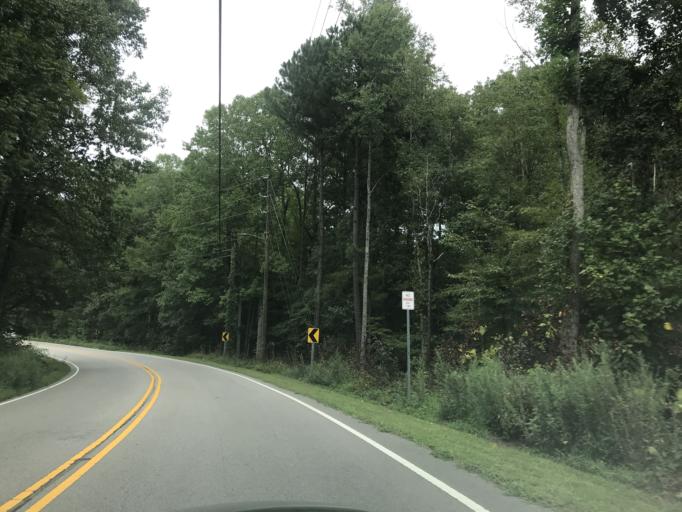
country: US
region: North Carolina
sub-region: Wake County
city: Apex
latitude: 35.7460
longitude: -78.8167
